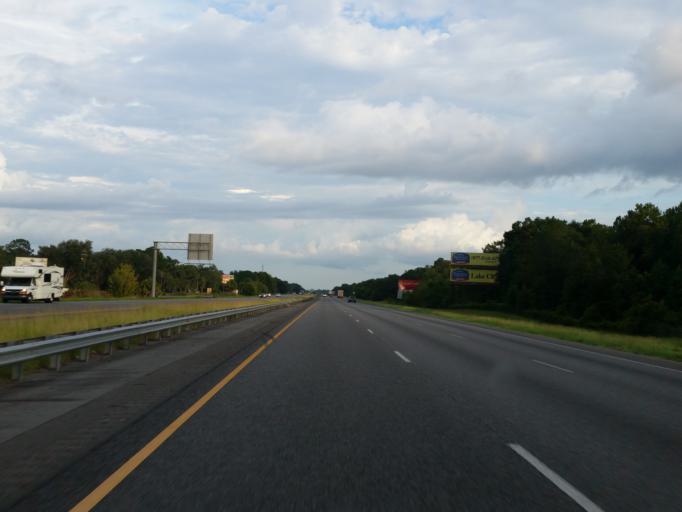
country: US
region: Georgia
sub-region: Lowndes County
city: Valdosta
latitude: 30.6737
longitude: -83.2169
